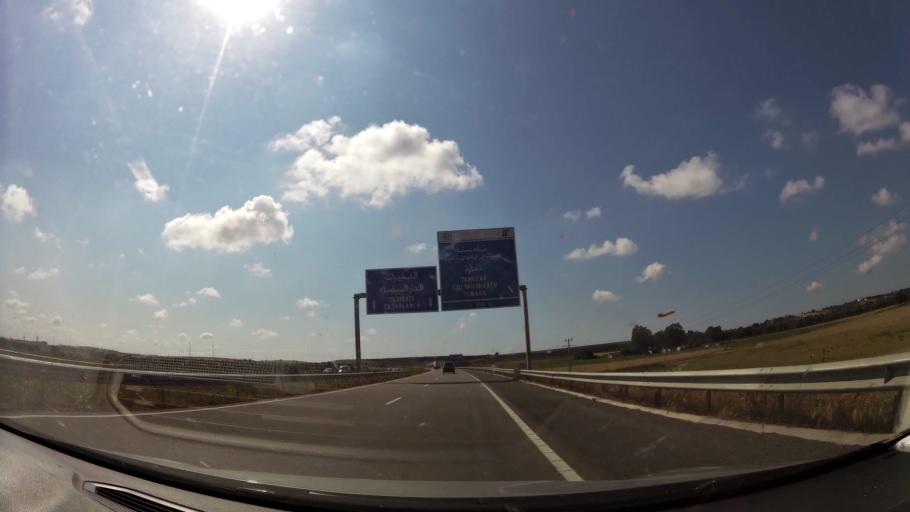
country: MA
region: Rabat-Sale-Zemmour-Zaer
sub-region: Skhirate-Temara
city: Temara
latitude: 33.8439
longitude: -6.8898
